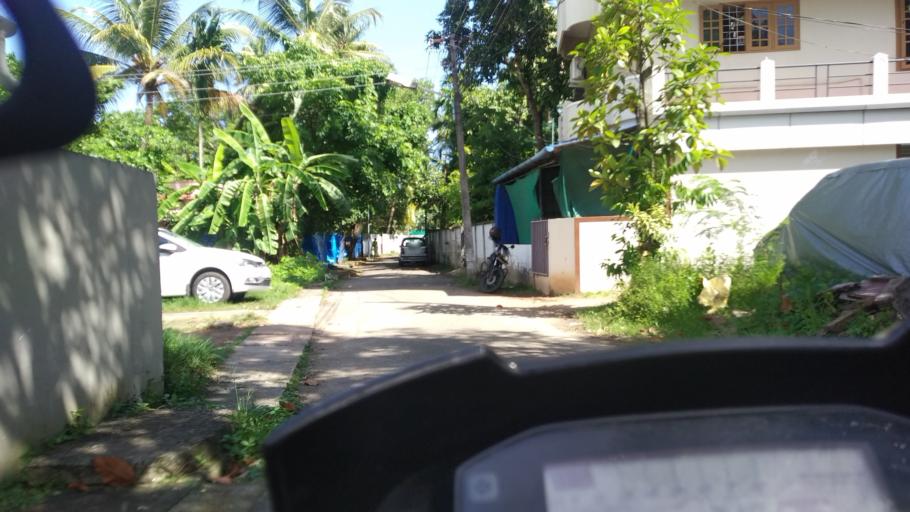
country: IN
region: Kerala
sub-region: Ernakulam
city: Elur
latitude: 10.0309
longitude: 76.2682
